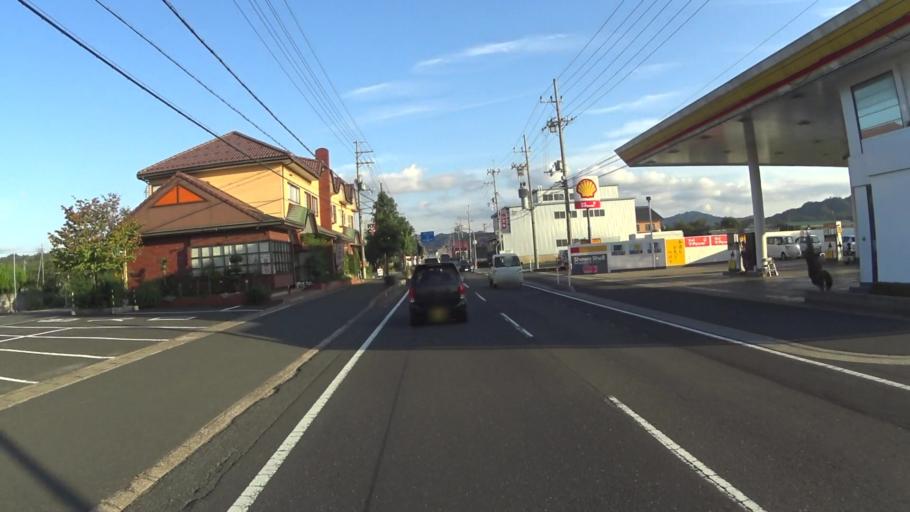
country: JP
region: Kyoto
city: Miyazu
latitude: 35.6004
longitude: 135.0868
